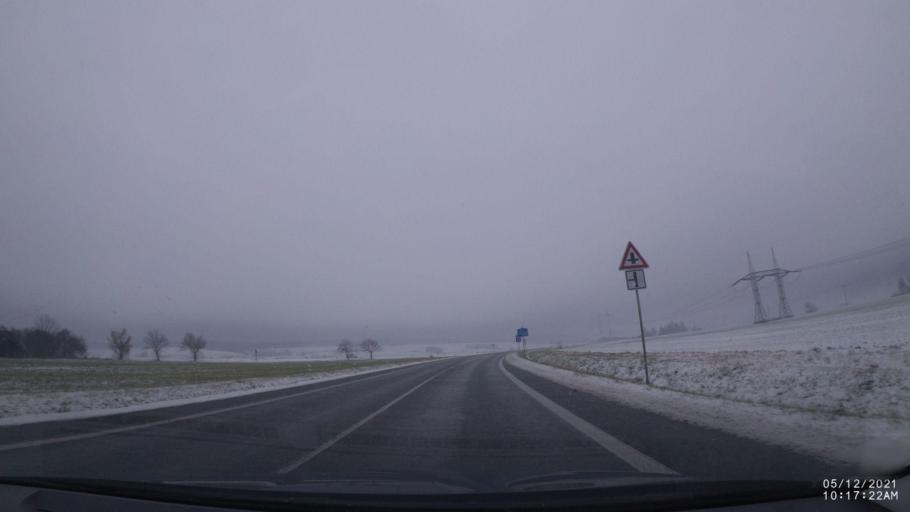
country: CZ
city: Vamberk
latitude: 50.1081
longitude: 16.2896
